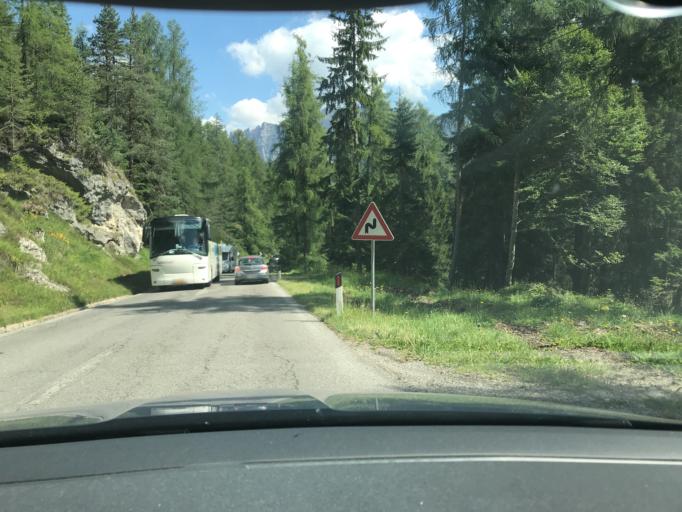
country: IT
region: Veneto
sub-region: Provincia di Belluno
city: Cortina d'Ampezzo
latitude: 46.5247
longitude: 12.1200
